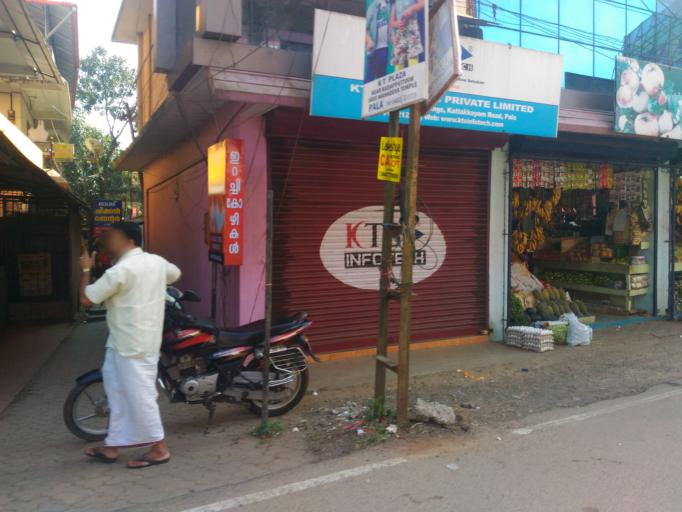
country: IN
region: Kerala
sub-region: Kottayam
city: Lalam
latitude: 9.7139
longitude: 76.6868
